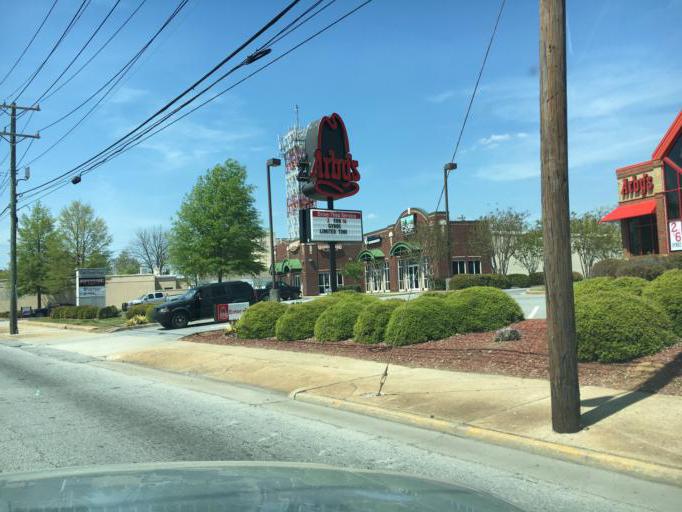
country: US
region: South Carolina
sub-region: Spartanburg County
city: Spartanburg
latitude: 34.9505
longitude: -81.9186
